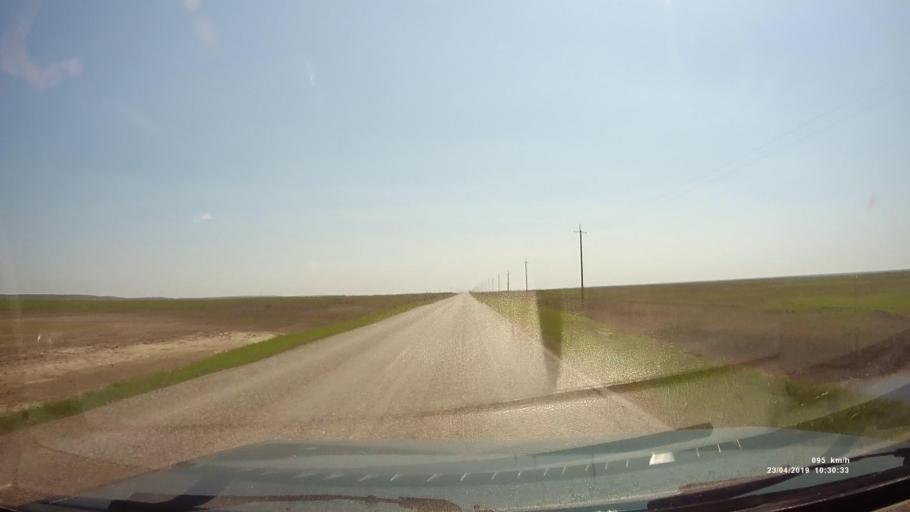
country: RU
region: Kalmykiya
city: Yashalta
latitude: 46.5914
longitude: 42.5466
